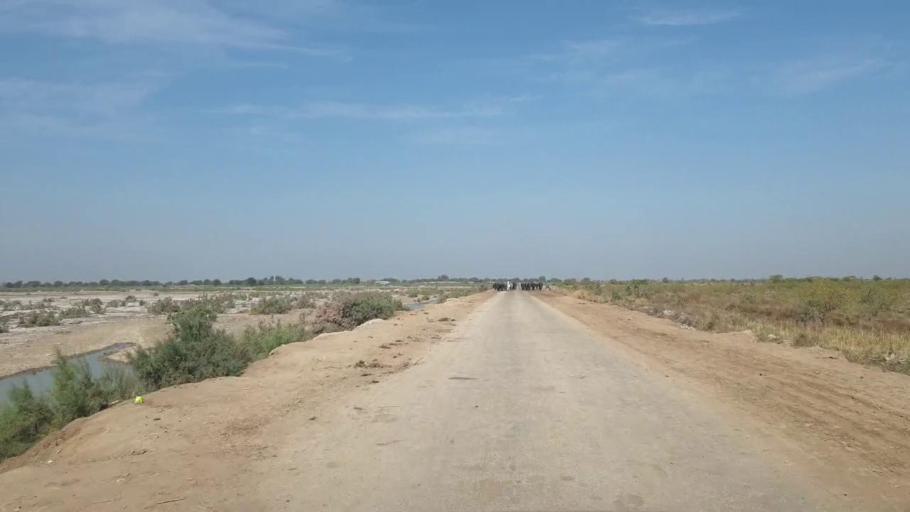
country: PK
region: Sindh
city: Samaro
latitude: 25.3675
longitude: 69.2597
